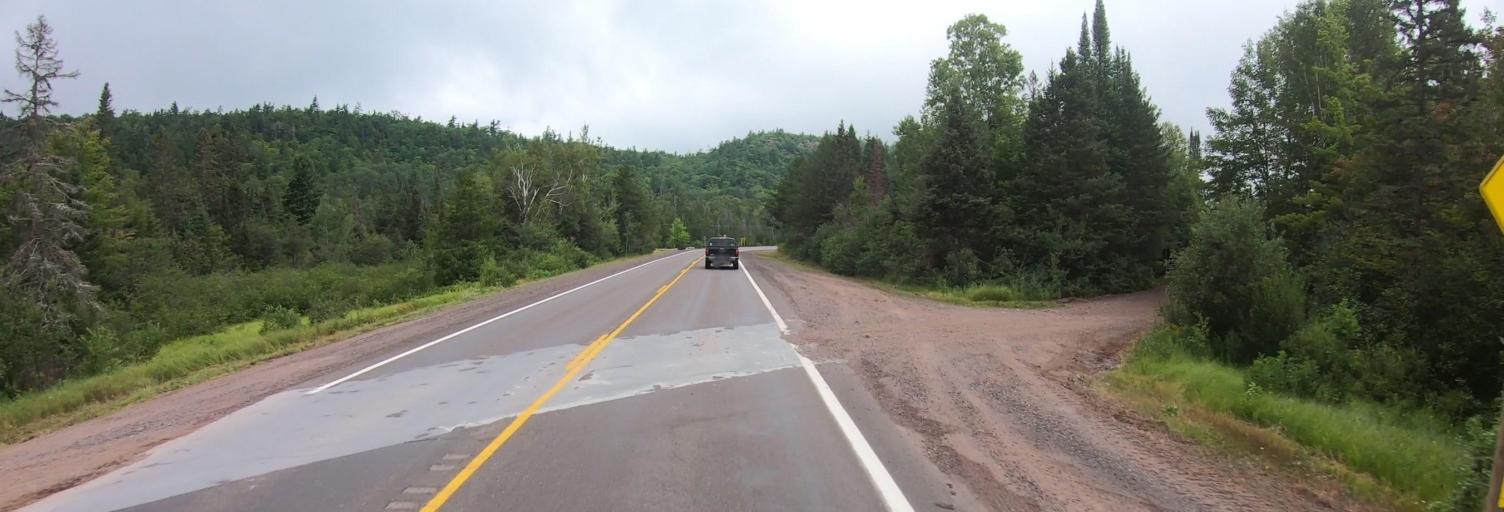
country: US
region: Michigan
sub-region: Keweenaw County
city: Eagle River
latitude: 47.3746
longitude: -88.3043
